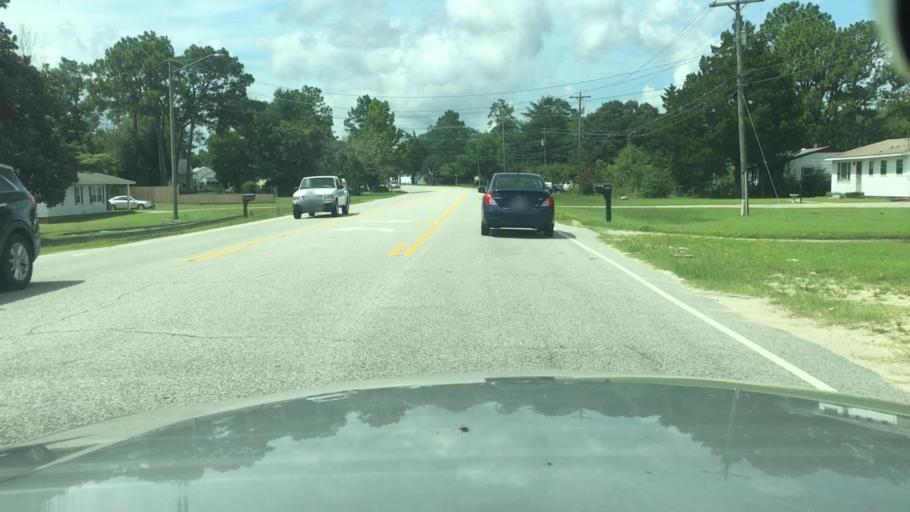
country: US
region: North Carolina
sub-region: Cumberland County
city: Hope Mills
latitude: 35.0208
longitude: -78.9342
